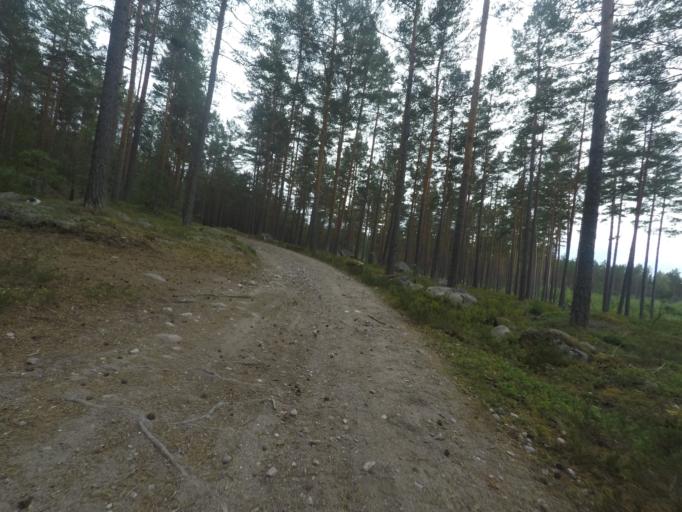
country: SE
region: Vaestmanland
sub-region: Kungsors Kommun
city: Kungsoer
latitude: 59.3689
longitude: 16.1073
